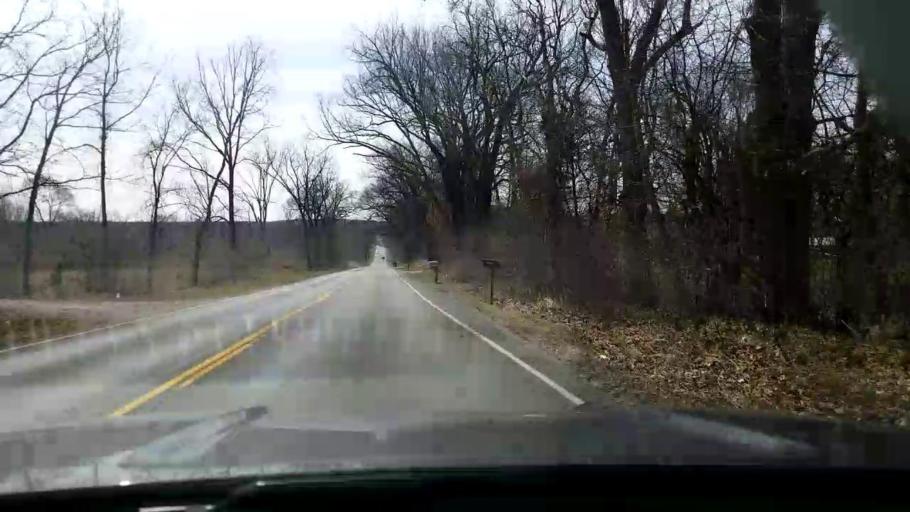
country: US
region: Michigan
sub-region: Jackson County
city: Spring Arbor
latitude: 42.2108
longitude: -84.5213
